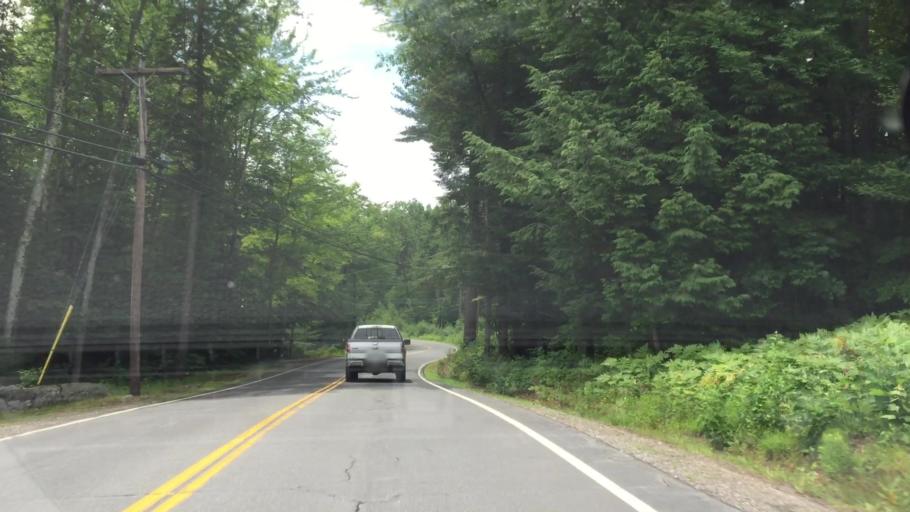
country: US
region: New Hampshire
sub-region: Grafton County
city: Holderness
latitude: 43.7590
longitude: -71.5571
